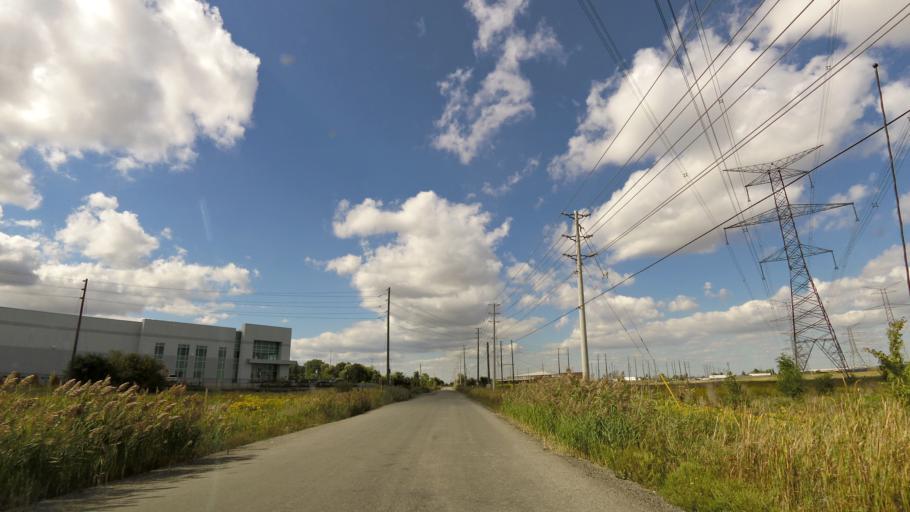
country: CA
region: Ontario
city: Brampton
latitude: 43.5951
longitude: -79.7919
